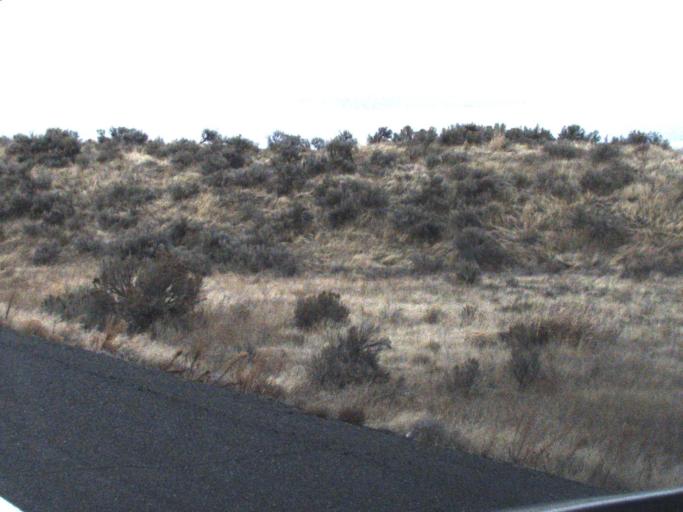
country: US
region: Washington
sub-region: Adams County
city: Ritzville
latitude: 46.7954
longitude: -118.4517
